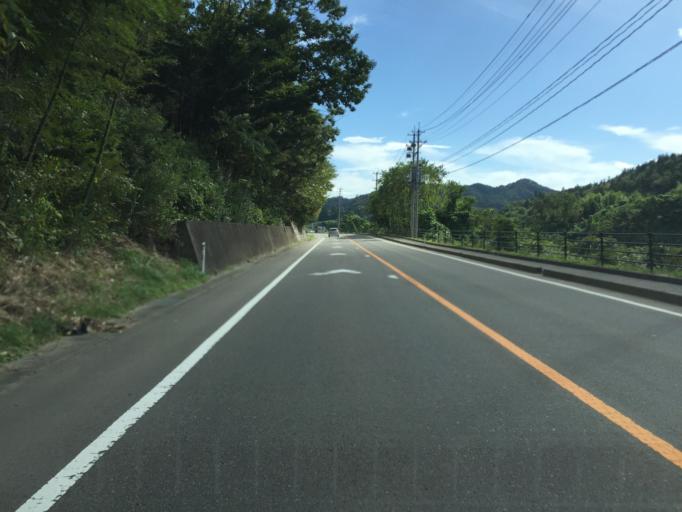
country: JP
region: Fukushima
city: Hobaramachi
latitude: 37.7962
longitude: 140.5731
